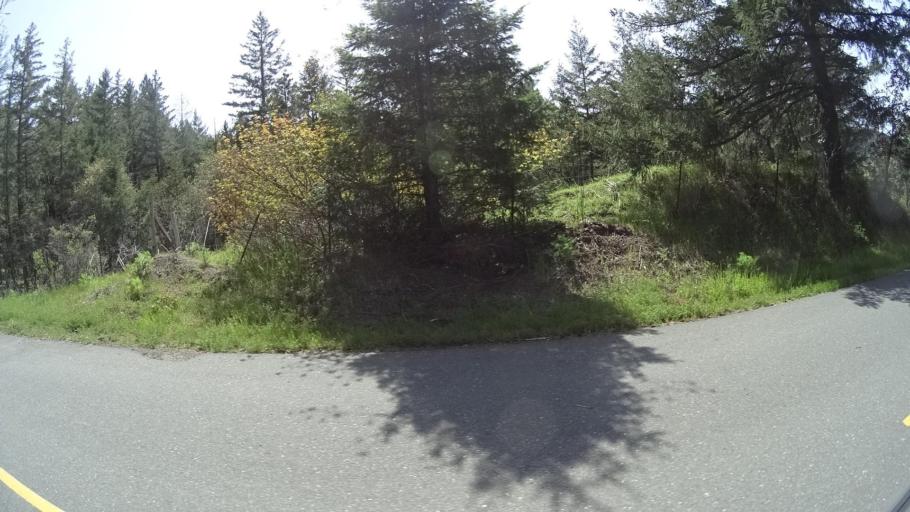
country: US
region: California
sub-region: Humboldt County
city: Redway
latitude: 40.4233
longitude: -123.7639
